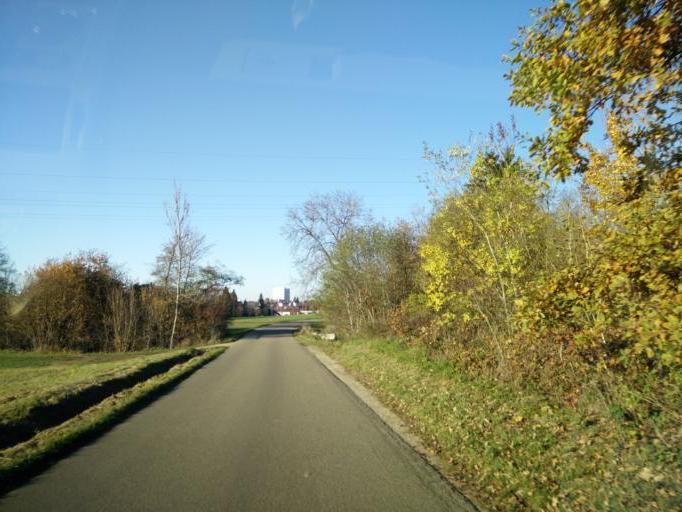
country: DE
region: Baden-Wuerttemberg
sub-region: Tuebingen Region
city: Gomaringen
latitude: 48.4448
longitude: 9.1031
